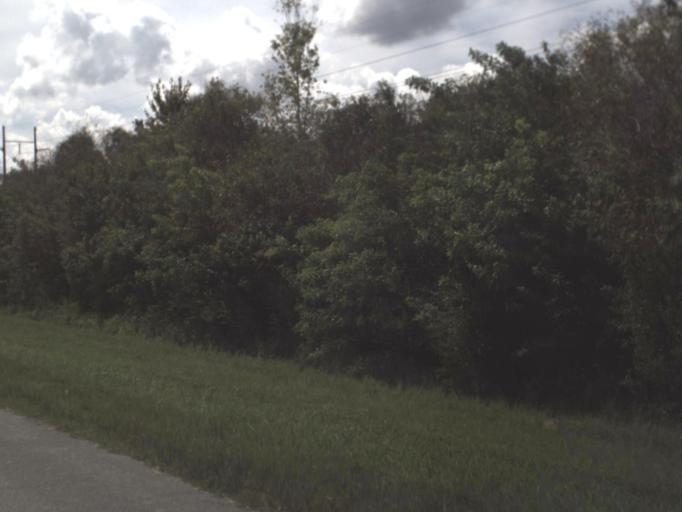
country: US
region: Florida
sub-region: Collier County
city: Orangetree
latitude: 26.0676
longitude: -81.3446
